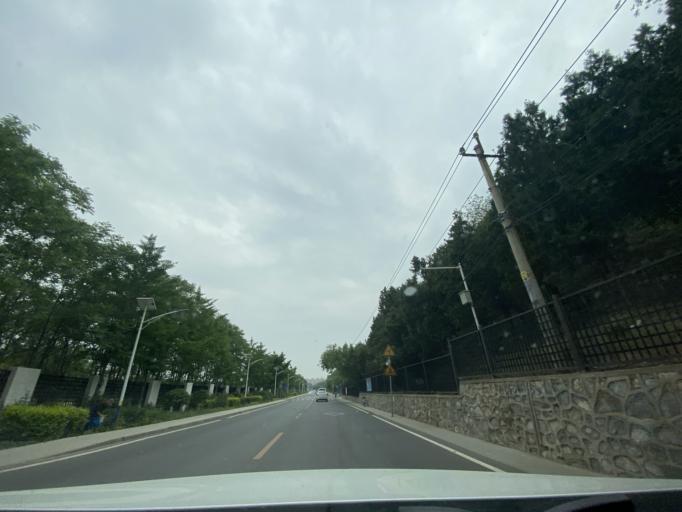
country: CN
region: Beijing
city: Sijiqing
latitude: 39.9384
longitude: 116.2393
